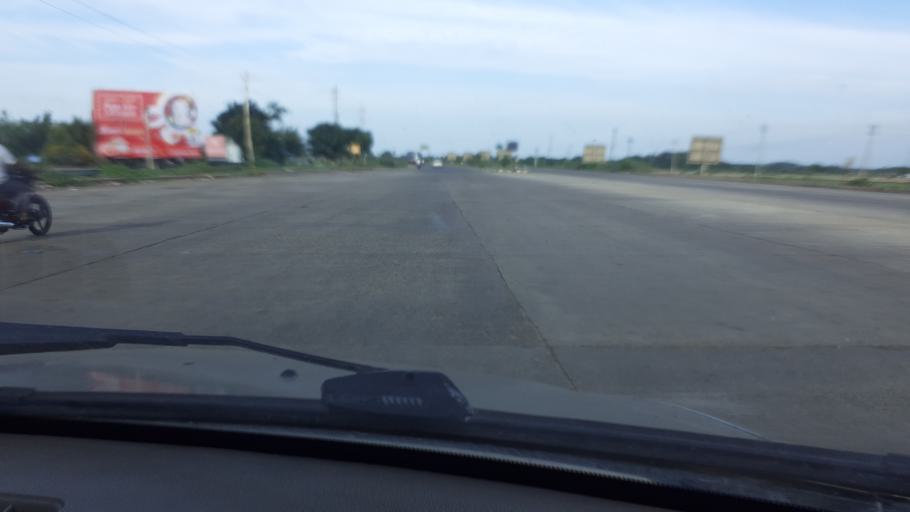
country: IN
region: Tamil Nadu
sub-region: Tirunelveli Kattabo
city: Nanguneri
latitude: 8.5276
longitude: 77.6637
